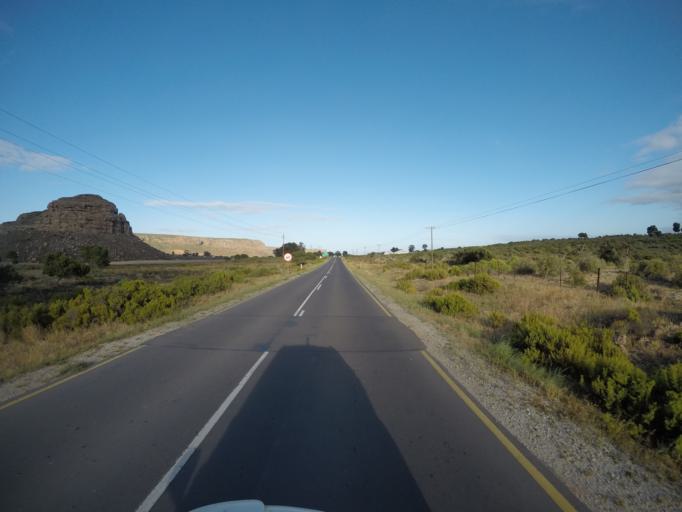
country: ZA
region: Western Cape
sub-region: West Coast District Municipality
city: Clanwilliam
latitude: -32.3130
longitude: 18.3596
